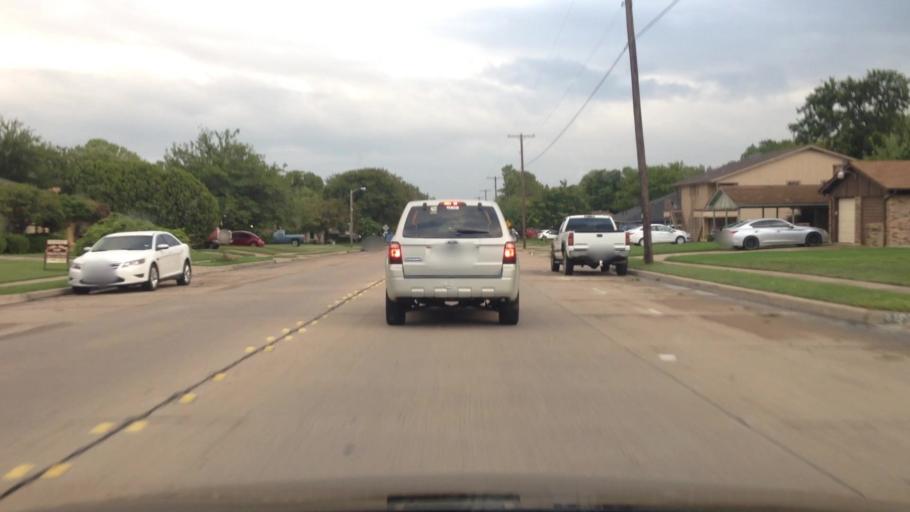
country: US
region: Texas
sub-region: Johnson County
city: Burleson
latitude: 32.5514
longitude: -97.3348
